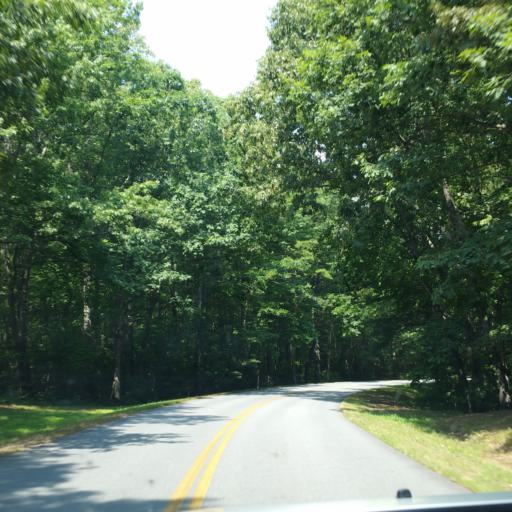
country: US
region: North Carolina
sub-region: Buncombe County
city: Bent Creek
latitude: 35.4998
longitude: -82.5763
